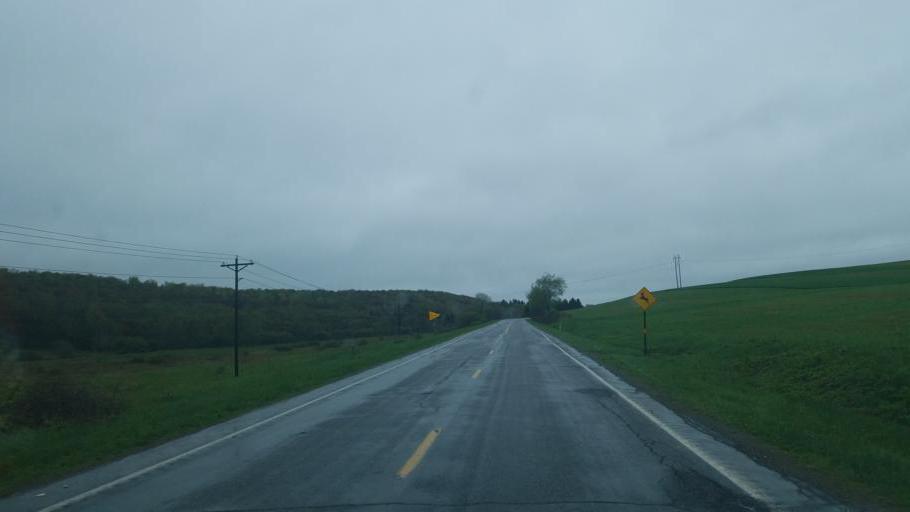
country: US
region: Pennsylvania
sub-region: Potter County
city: Coudersport
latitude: 41.8665
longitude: -77.8453
